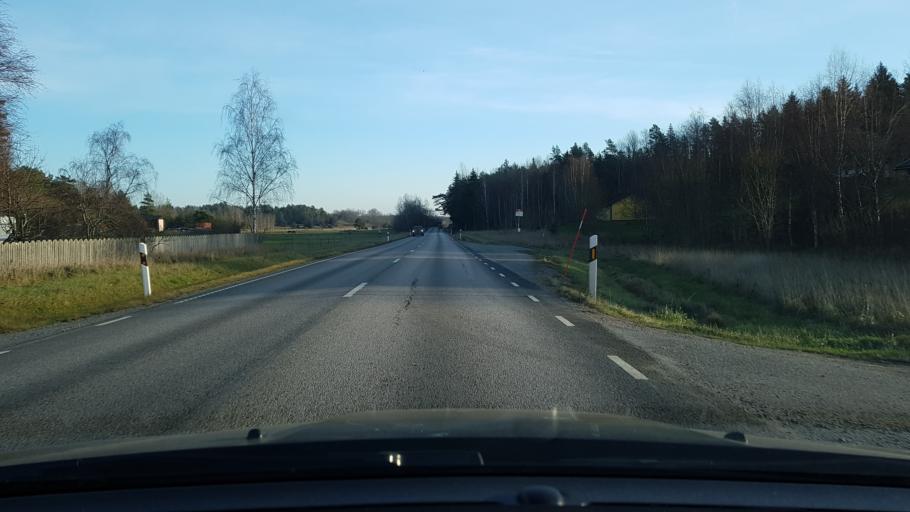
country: SE
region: Stockholm
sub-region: Norrtalje Kommun
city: Nykvarn
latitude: 59.7444
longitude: 18.1201
